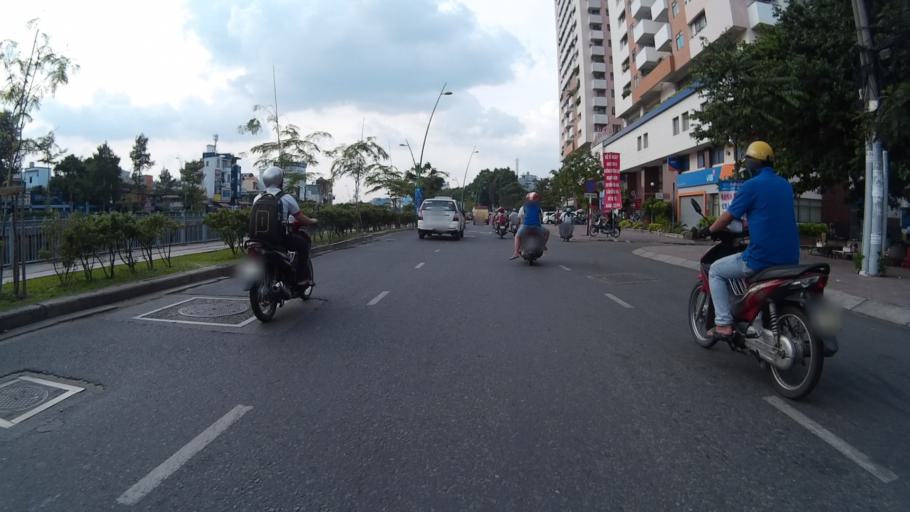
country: VN
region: Ho Chi Minh City
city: Quan Phu Nhuan
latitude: 10.7858
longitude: 106.6760
